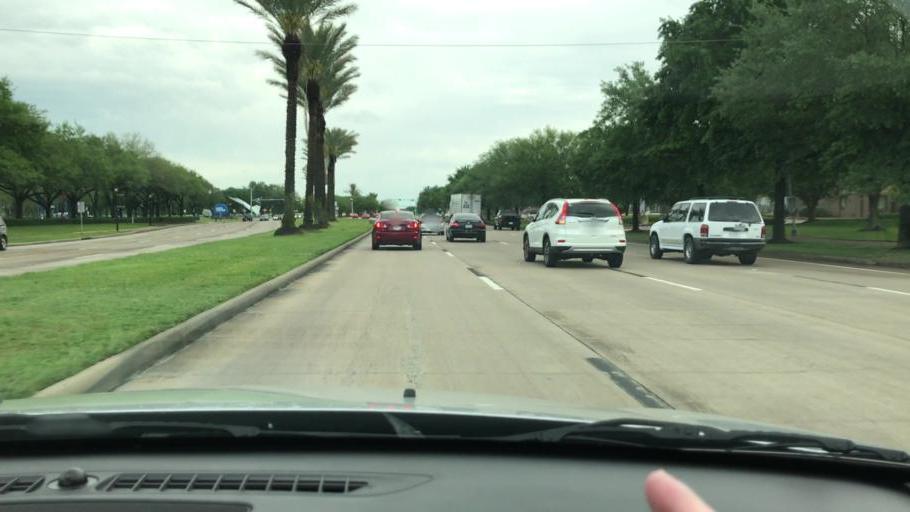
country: US
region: Texas
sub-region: Harris County
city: Nassau Bay
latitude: 29.5485
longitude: -95.0980
